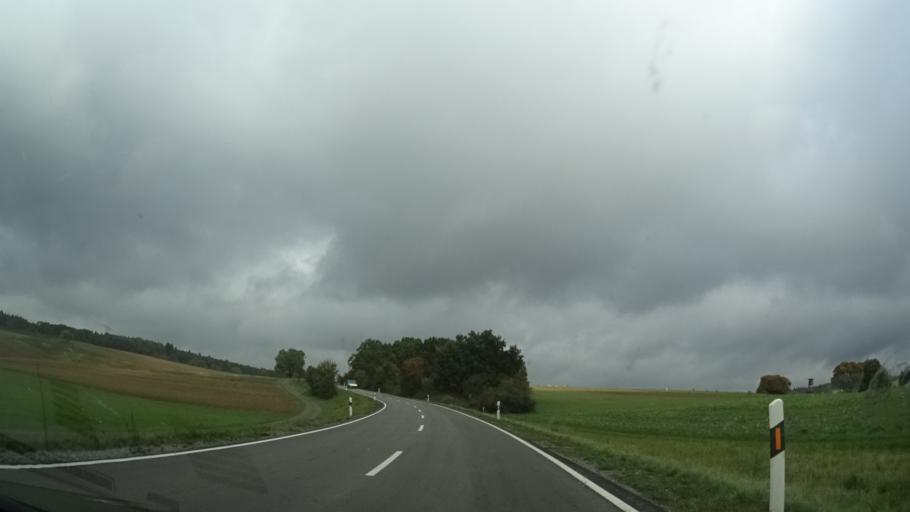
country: DE
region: Baden-Wuerttemberg
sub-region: Karlsruhe Region
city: Konigsbach-Stein
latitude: 48.9787
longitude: 8.6385
